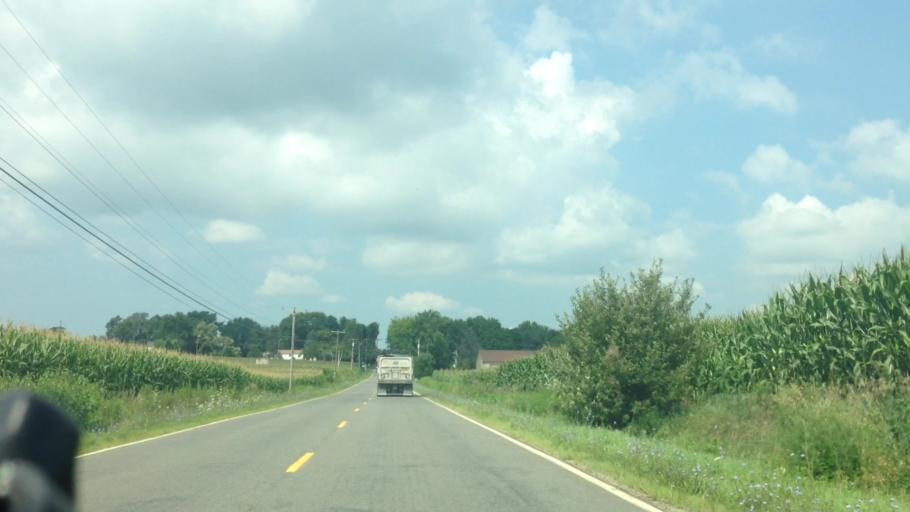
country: US
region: Ohio
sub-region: Stark County
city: Canal Fulton
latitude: 40.8536
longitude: -81.6434
